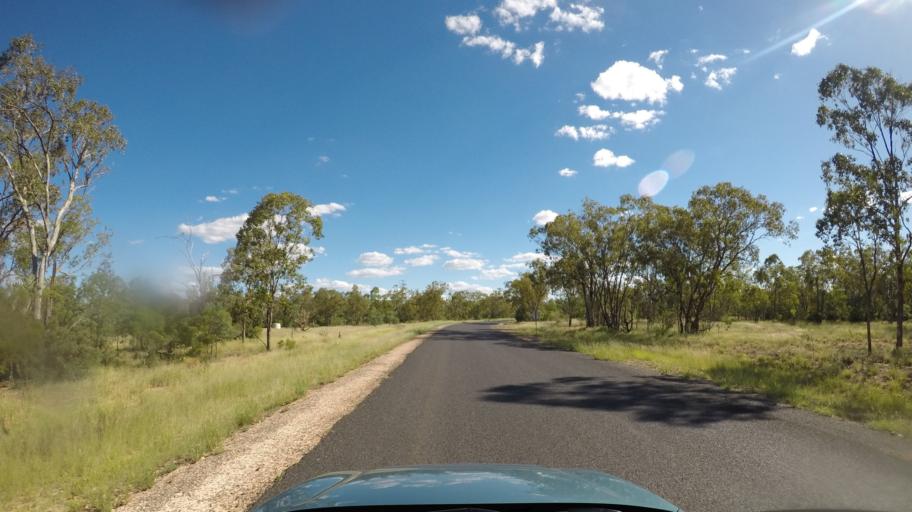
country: AU
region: Queensland
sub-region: Goondiwindi
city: Goondiwindi
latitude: -28.1724
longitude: 150.4720
